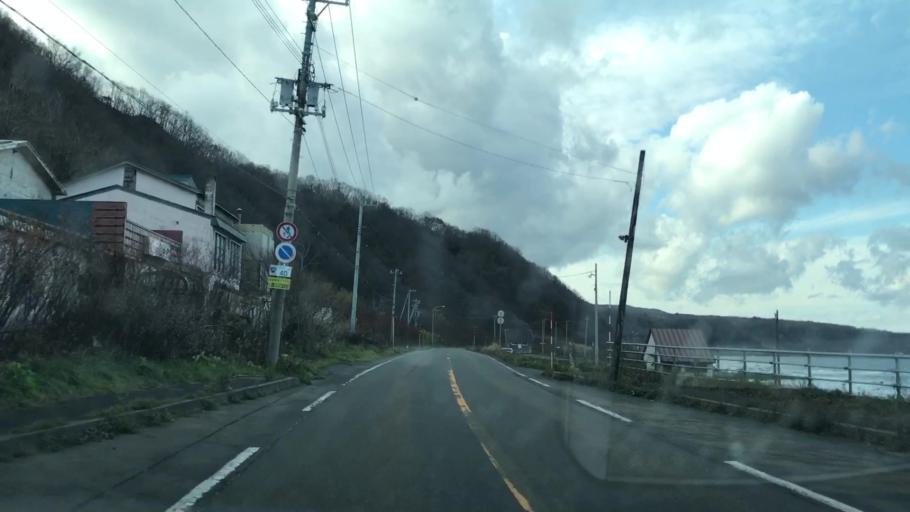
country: JP
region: Hokkaido
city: Yoichi
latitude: 43.3342
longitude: 140.4451
